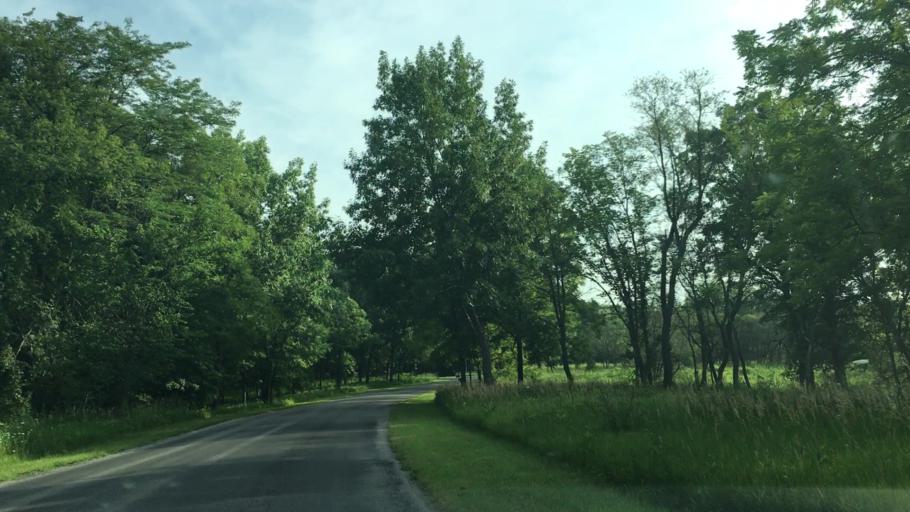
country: US
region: Iowa
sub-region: Johnson County
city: Tiffin
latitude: 41.7237
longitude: -91.7248
